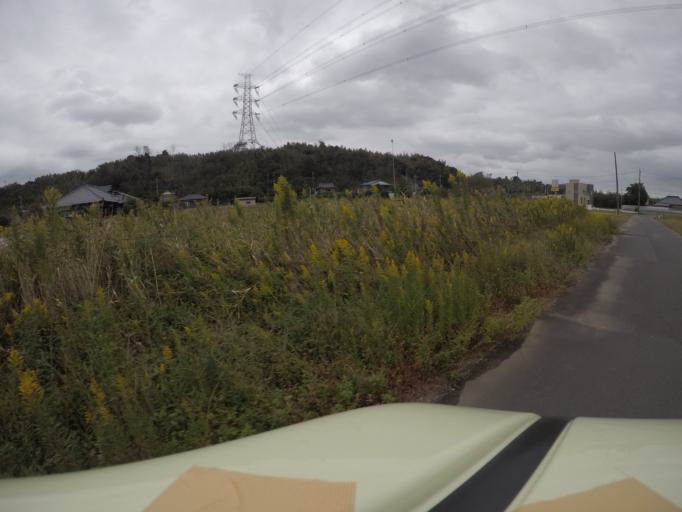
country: JP
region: Ibaraki
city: Itako
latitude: 35.9632
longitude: 140.5078
